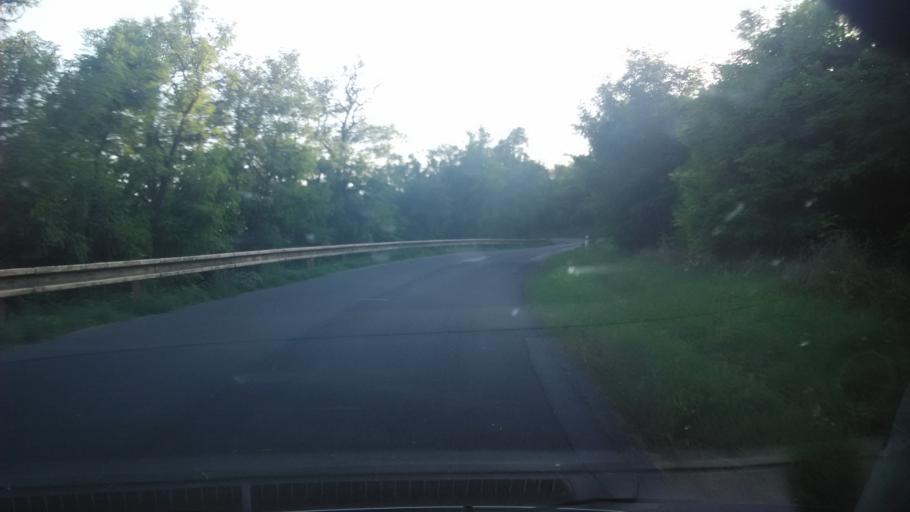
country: SK
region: Banskobystricky
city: Dudince
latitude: 48.0538
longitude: 18.8035
